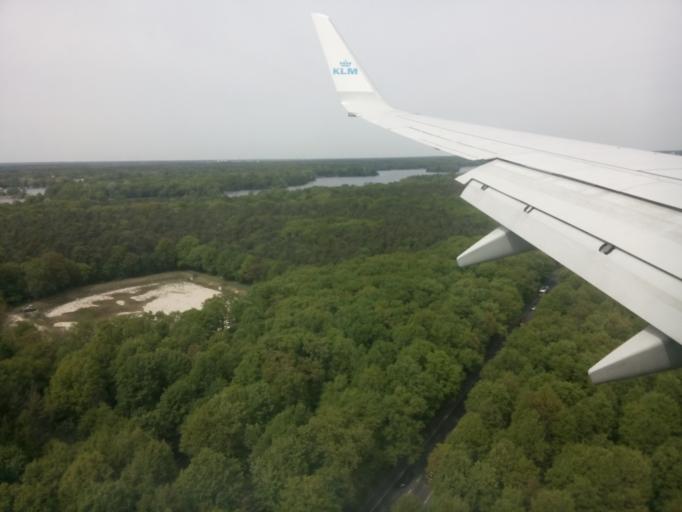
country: DE
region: Berlin
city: Haselhorst
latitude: 52.5562
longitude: 13.2511
